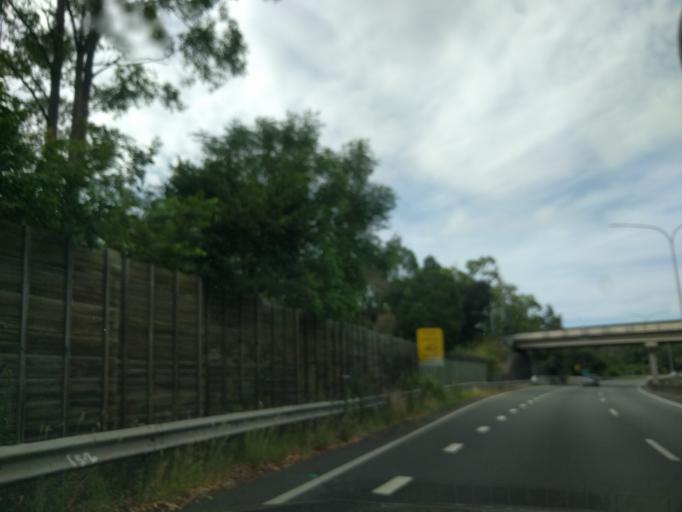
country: AU
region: Queensland
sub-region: Brisbane
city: Kenmore Hills
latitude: -27.5164
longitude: 152.9557
